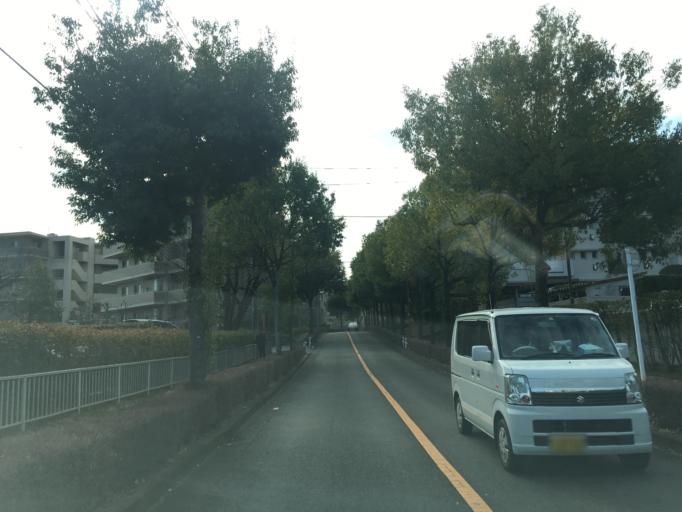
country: JP
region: Tokyo
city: Hino
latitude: 35.6191
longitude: 139.4350
